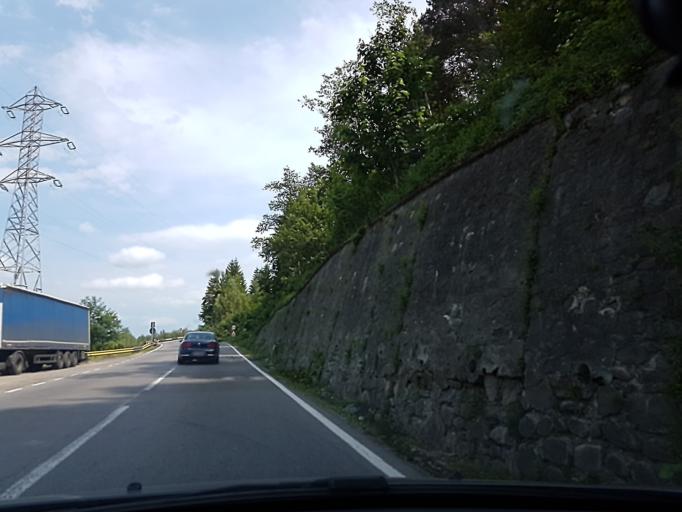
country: RO
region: Prahova
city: Maneciu
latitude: 45.3355
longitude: 25.9647
